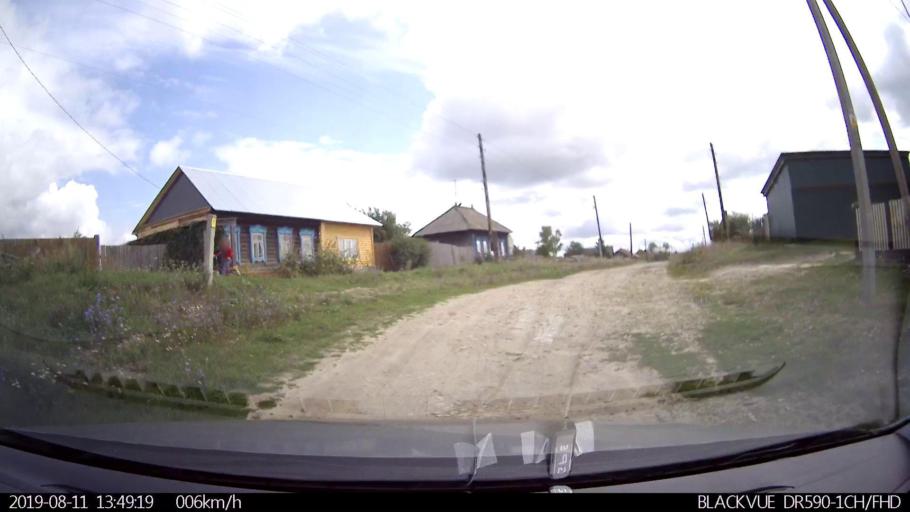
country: RU
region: Ulyanovsk
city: Ignatovka
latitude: 53.8477
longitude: 47.5804
